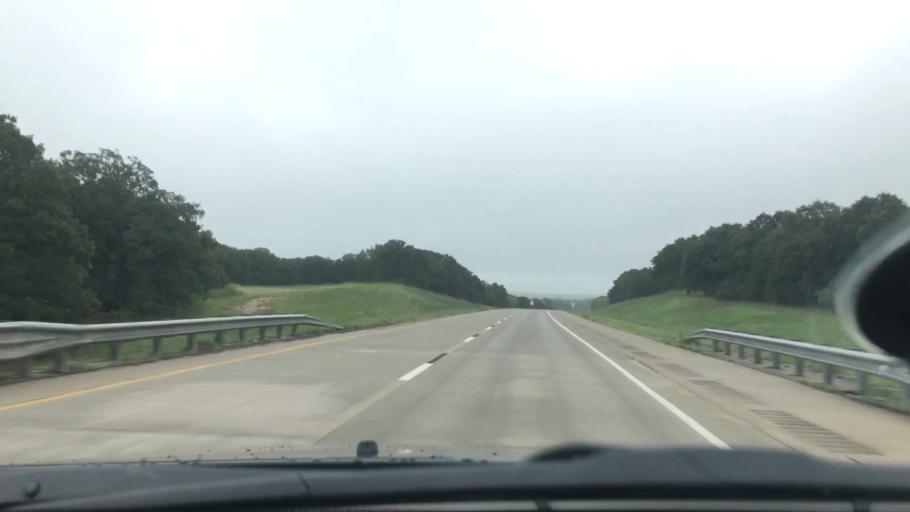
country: US
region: Oklahoma
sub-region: Okfuskee County
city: Boley
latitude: 35.3838
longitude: -96.5651
